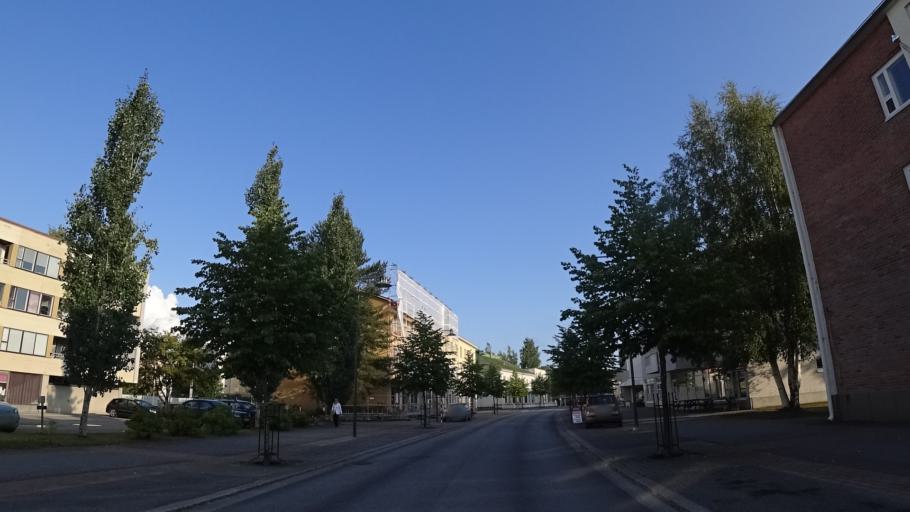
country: FI
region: North Karelia
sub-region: Pielisen Karjala
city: Lieksa
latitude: 63.3161
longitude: 30.0321
